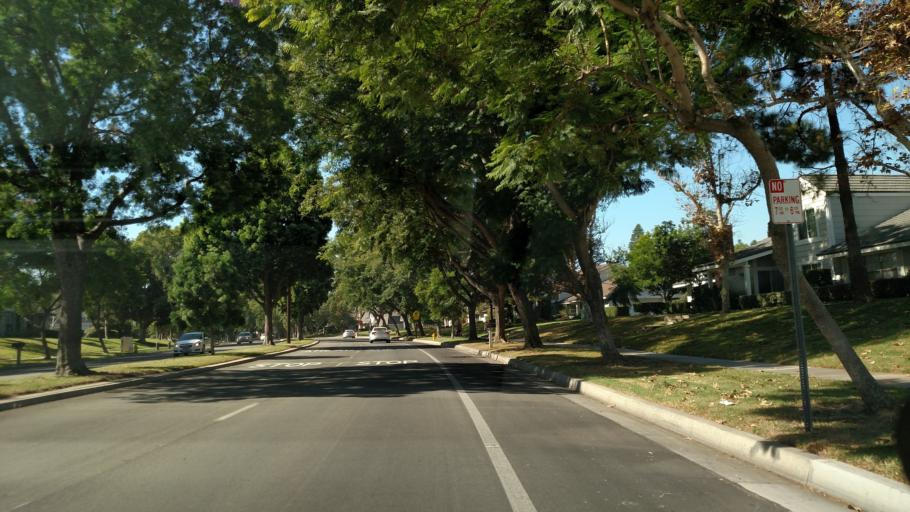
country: US
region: California
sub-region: Orange County
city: Irvine
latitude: 33.6881
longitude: -117.8008
